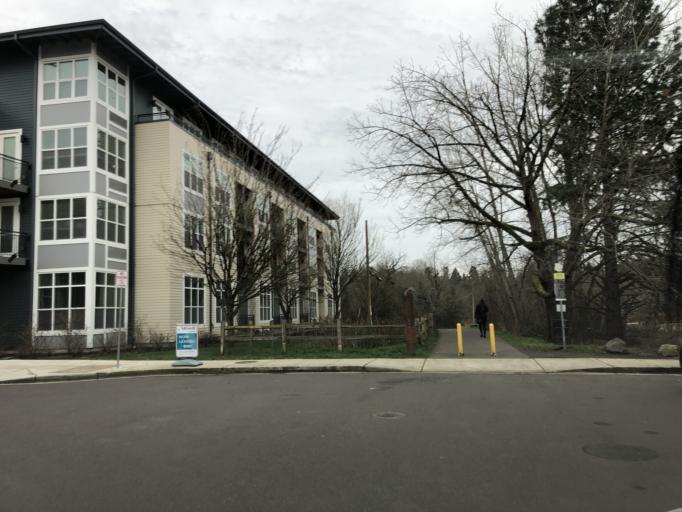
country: US
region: Oregon
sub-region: Washington County
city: Tigard
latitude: 45.4276
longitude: -122.7706
